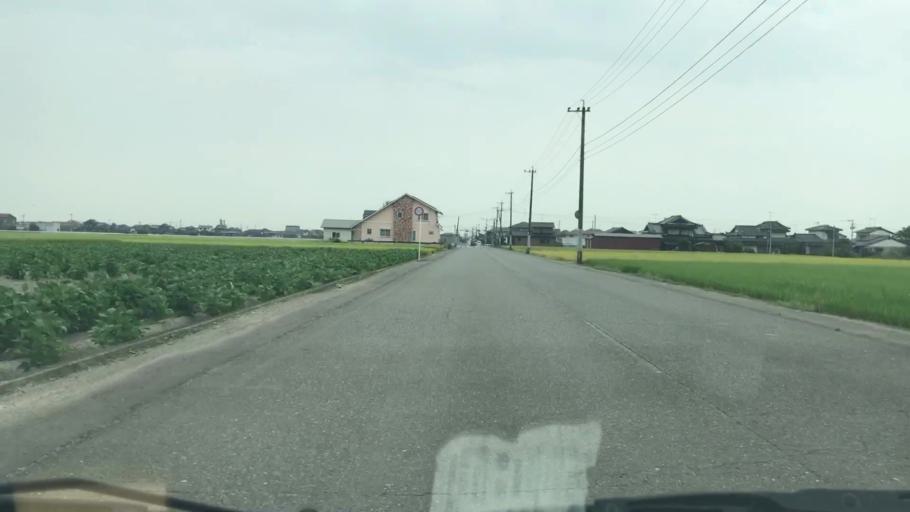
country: JP
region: Saga Prefecture
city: Saga-shi
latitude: 33.2230
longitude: 130.1769
